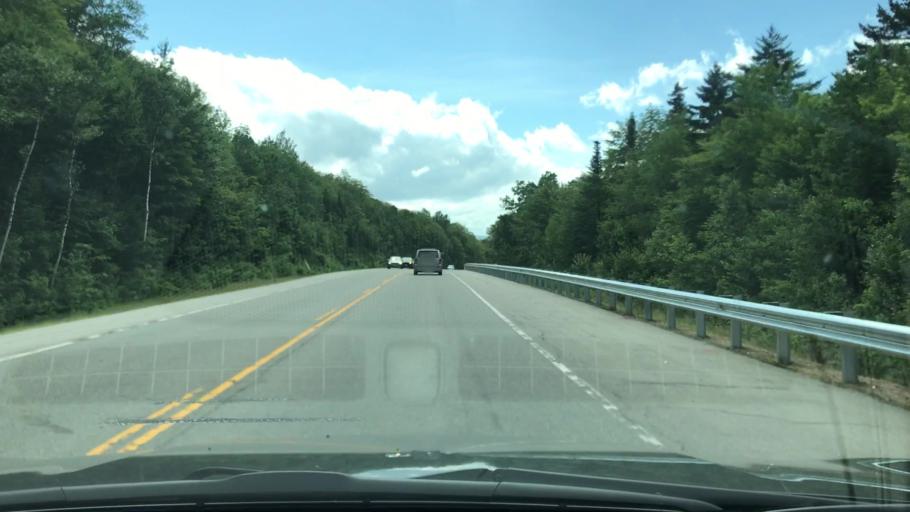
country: US
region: New Hampshire
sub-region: Coos County
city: Gorham
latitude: 44.3683
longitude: -71.3065
